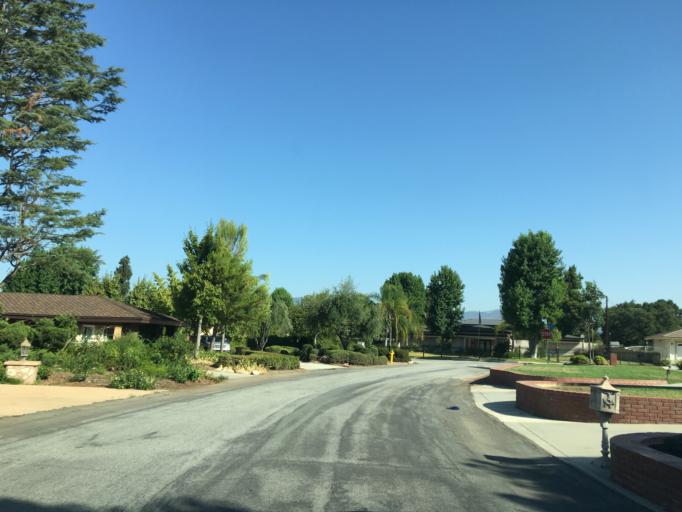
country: US
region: California
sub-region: Los Angeles County
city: Charter Oak
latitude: 34.0851
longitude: -117.8438
